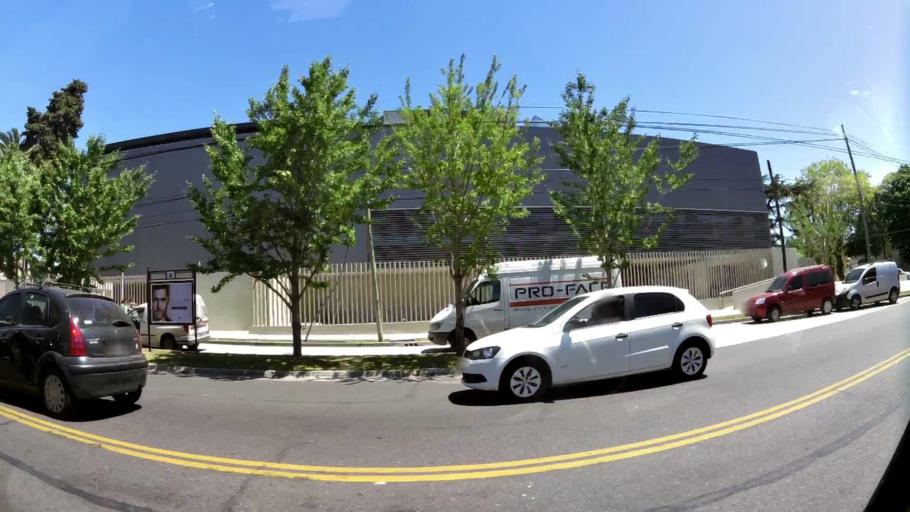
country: AR
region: Buenos Aires
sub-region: Partido de San Isidro
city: San Isidro
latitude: -34.4924
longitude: -58.5232
